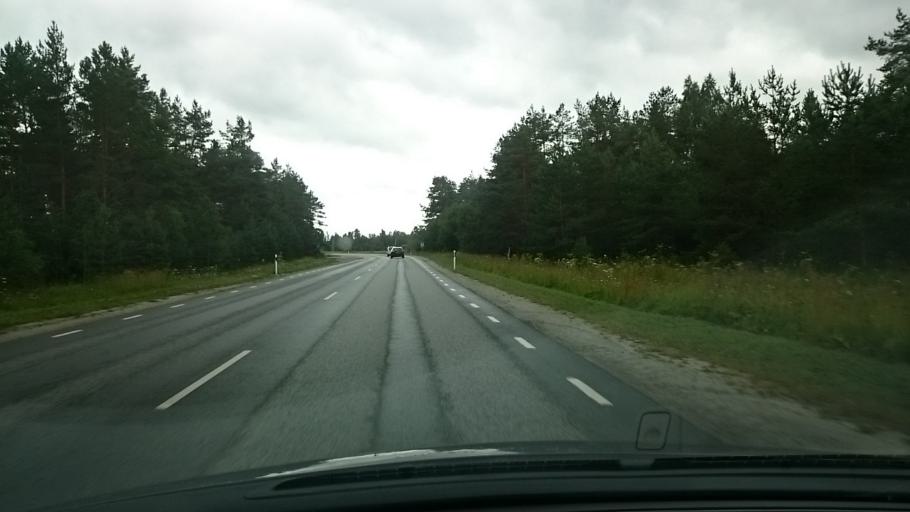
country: EE
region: Harju
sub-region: Keila linn
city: Keila
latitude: 59.2694
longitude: 24.2933
